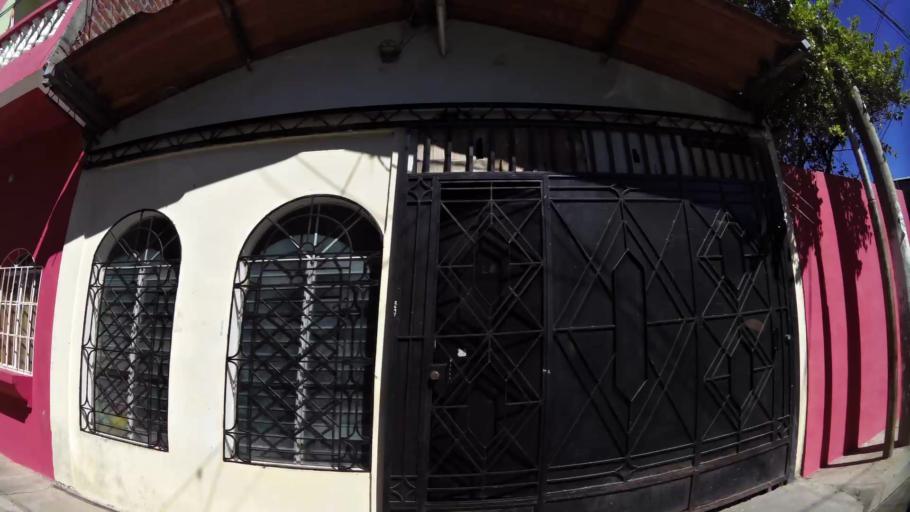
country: SV
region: San Miguel
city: San Miguel
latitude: 13.4932
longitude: -88.1655
